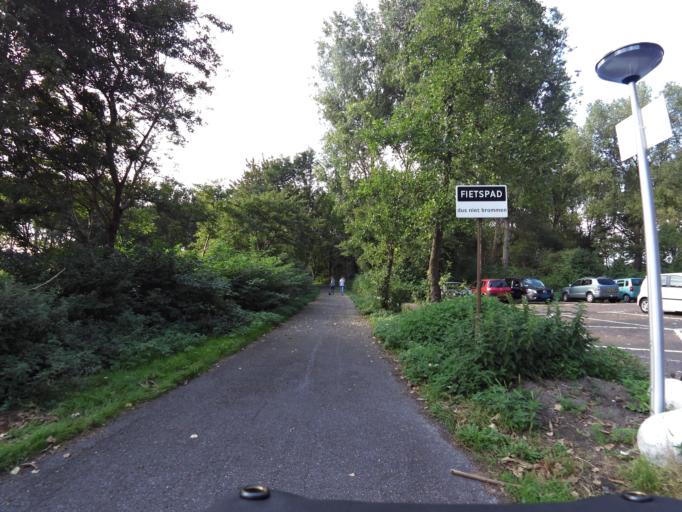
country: NL
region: South Holland
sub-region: Gemeente Maassluis
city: Maassluis
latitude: 51.9053
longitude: 4.2802
